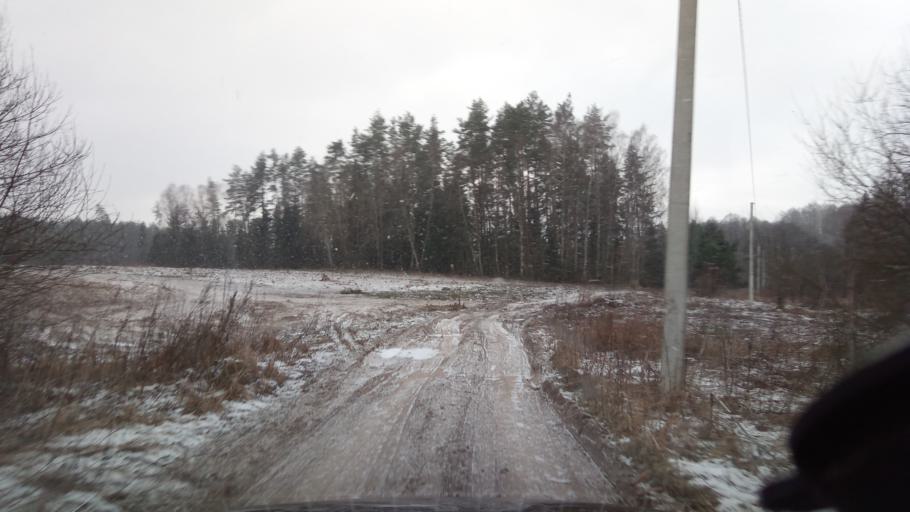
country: LT
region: Alytaus apskritis
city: Varena
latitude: 54.1280
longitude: 24.6781
